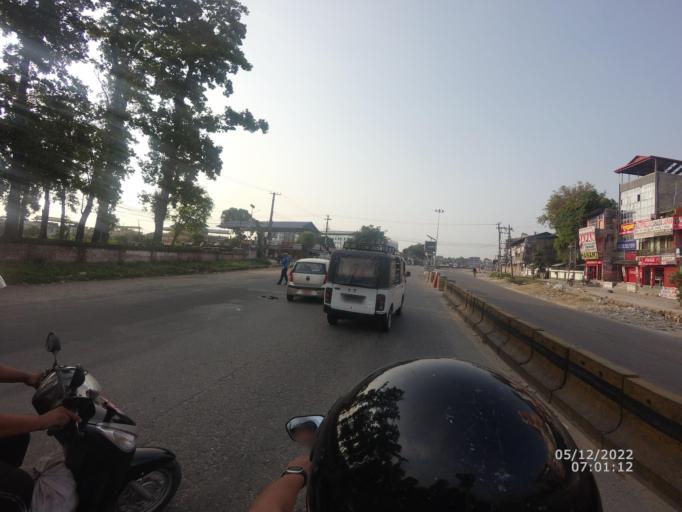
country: NP
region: Central Region
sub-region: Narayani Zone
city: Bharatpur
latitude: 27.6873
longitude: 84.4290
